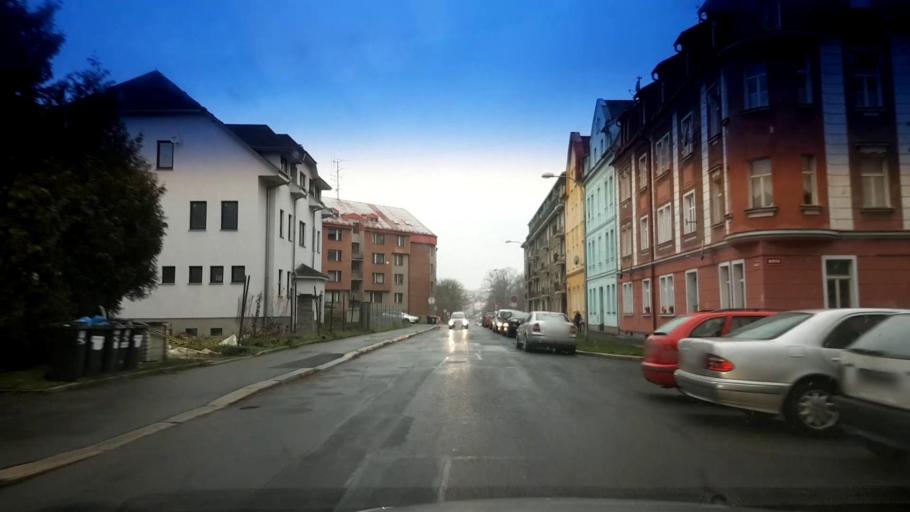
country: CZ
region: Karlovarsky
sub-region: Okres Cheb
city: Cheb
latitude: 50.0711
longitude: 12.3758
